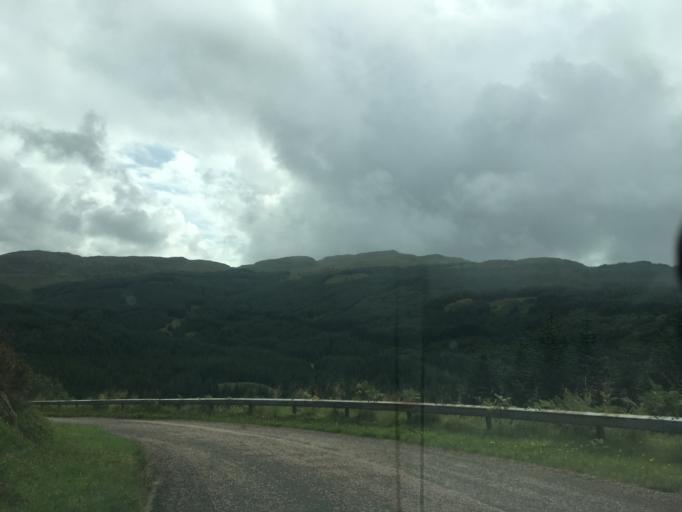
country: GB
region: Scotland
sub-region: Argyll and Bute
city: Oban
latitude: 56.2490
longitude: -5.4307
